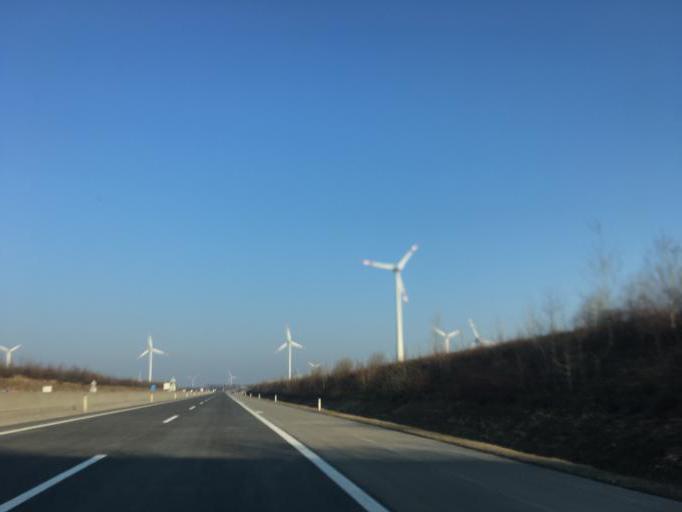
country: AT
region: Burgenland
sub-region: Politischer Bezirk Neusiedl am See
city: Potzneusiedl
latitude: 48.0348
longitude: 16.9143
